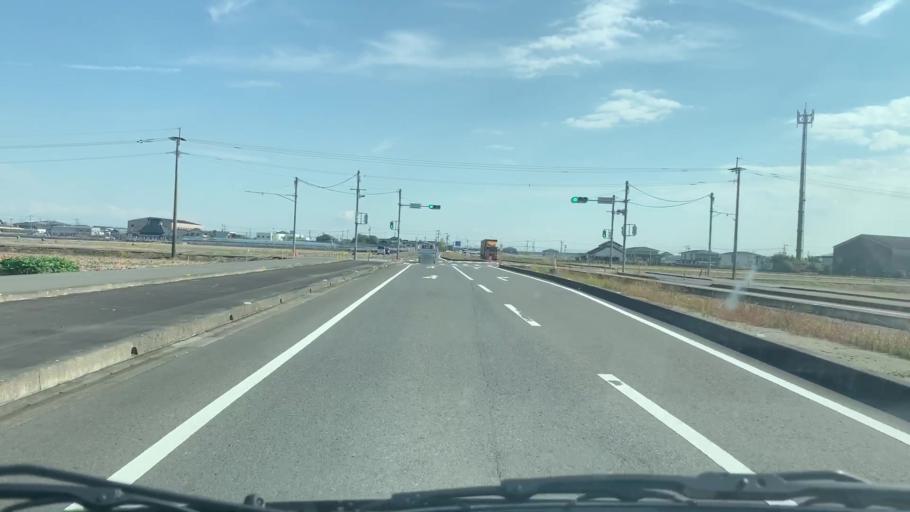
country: JP
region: Saga Prefecture
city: Saga-shi
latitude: 33.2214
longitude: 130.2034
